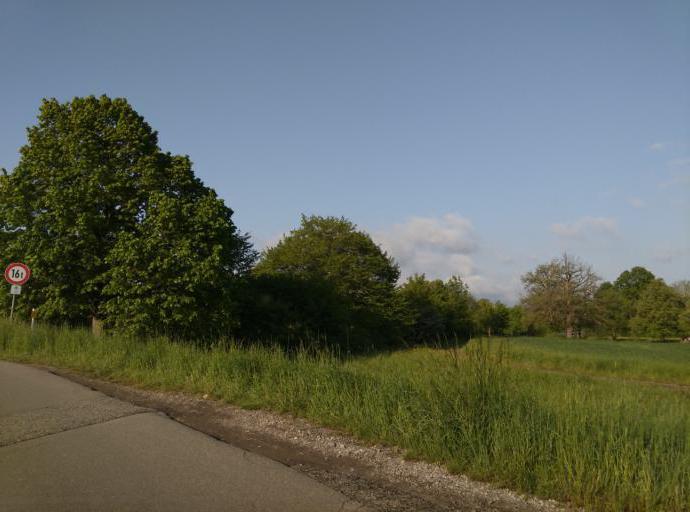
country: DE
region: Baden-Wuerttemberg
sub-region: Tuebingen Region
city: Wannweil
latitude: 48.4977
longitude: 9.1364
